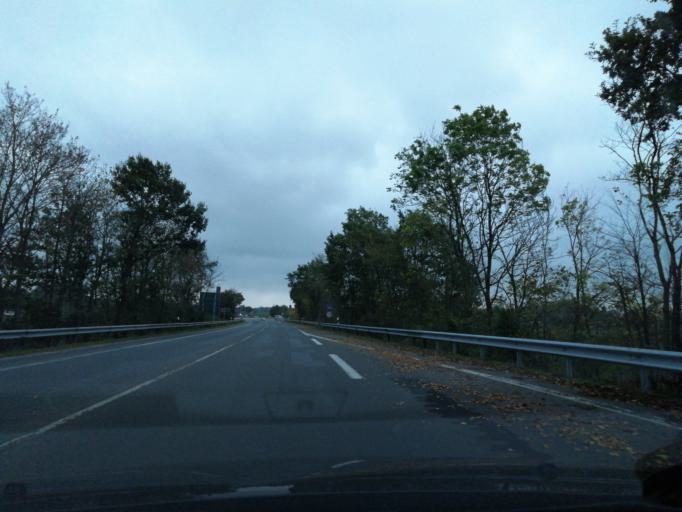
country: DE
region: Lower Saxony
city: Fedderwarden
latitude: 53.5434
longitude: 8.0510
